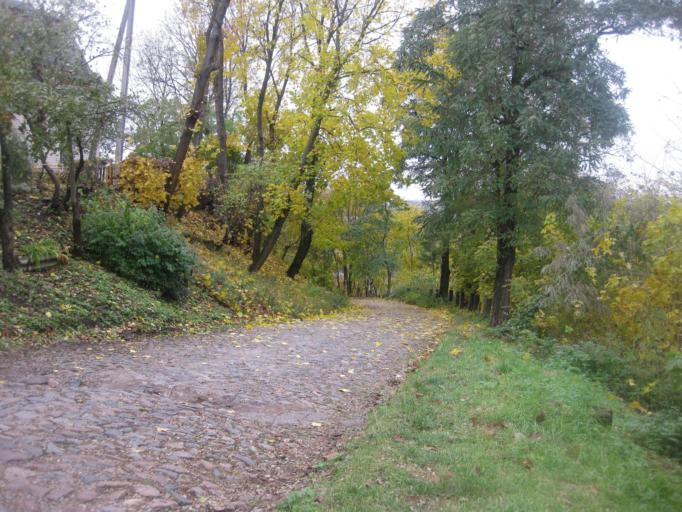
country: LT
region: Kauno apskritis
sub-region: Kaunas
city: Kaunas
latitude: 54.9091
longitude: 23.9099
